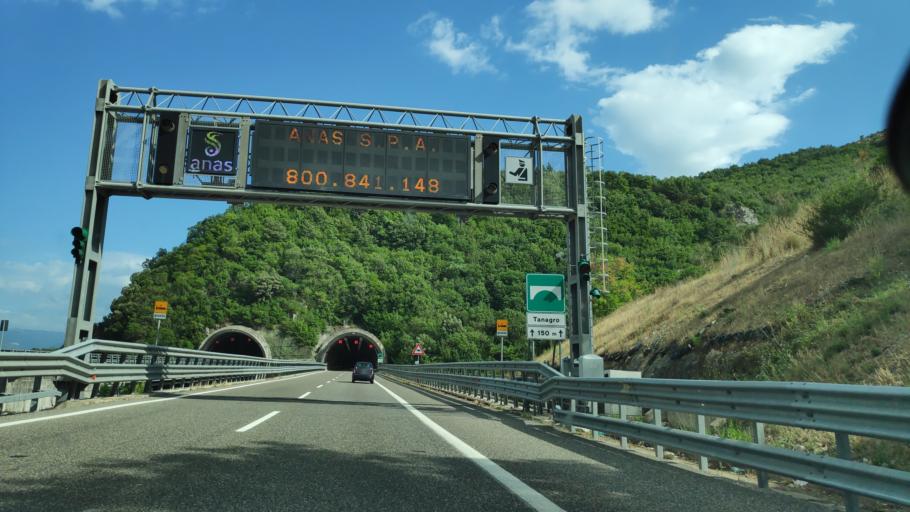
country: IT
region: Campania
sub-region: Provincia di Salerno
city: Sicignano degli Alburni
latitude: 40.6059
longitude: 15.2996
